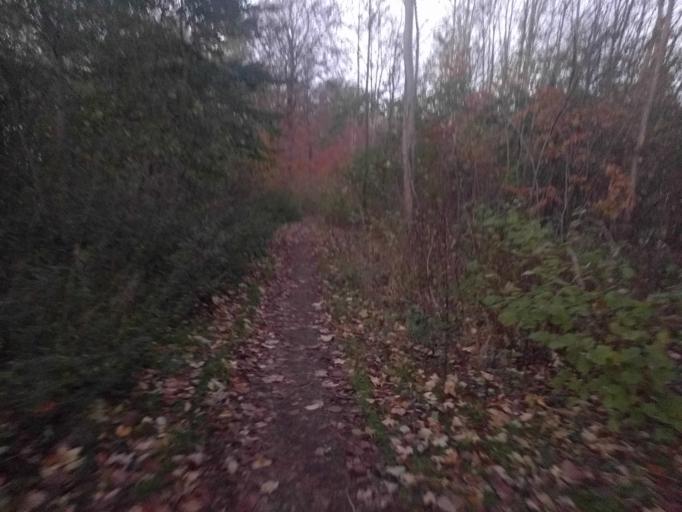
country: DK
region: South Denmark
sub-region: Fredericia Kommune
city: Snoghoj
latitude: 55.5390
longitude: 9.7217
